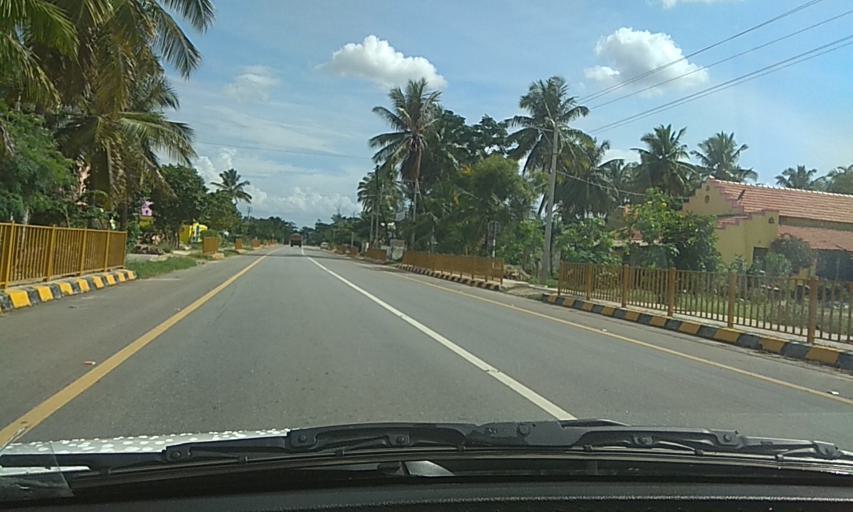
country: IN
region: Karnataka
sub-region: Mandya
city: Maddur
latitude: 12.6626
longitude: 77.0531
